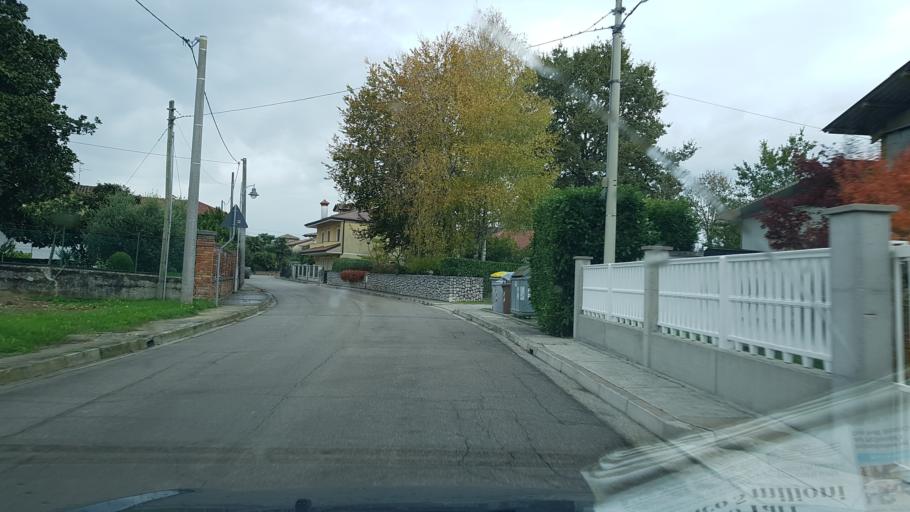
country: IT
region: Friuli Venezia Giulia
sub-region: Provincia di Udine
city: Fiumicello
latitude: 45.8013
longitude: 13.4024
